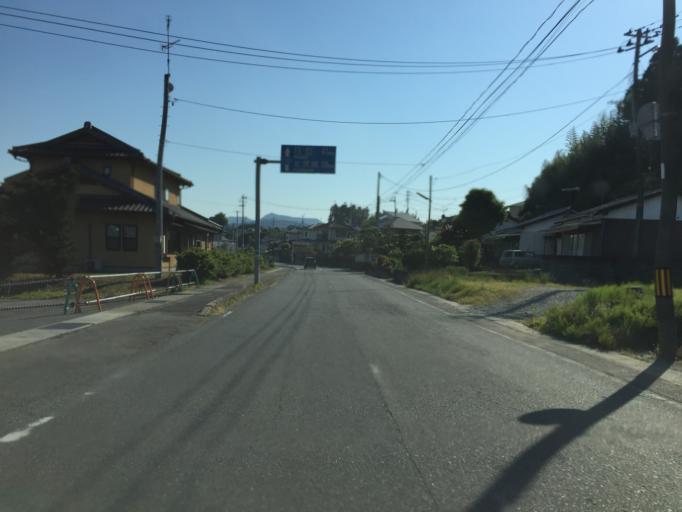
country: JP
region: Ibaraki
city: Kitaibaraki
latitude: 36.8917
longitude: 140.7561
